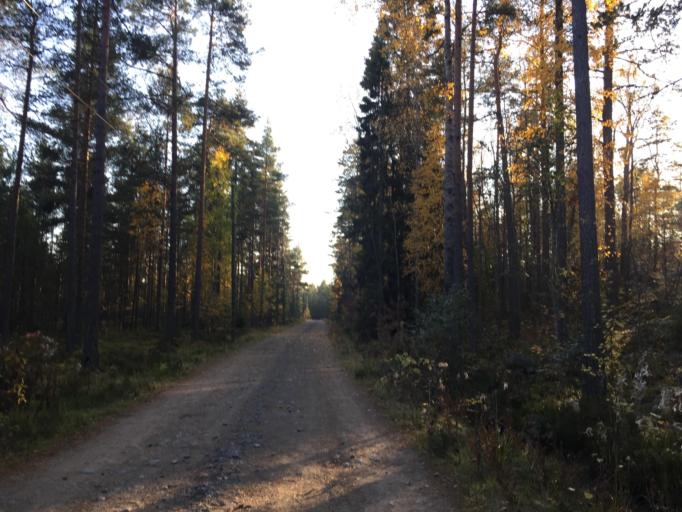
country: RU
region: Leningrad
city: Priozersk
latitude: 61.2830
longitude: 30.1035
